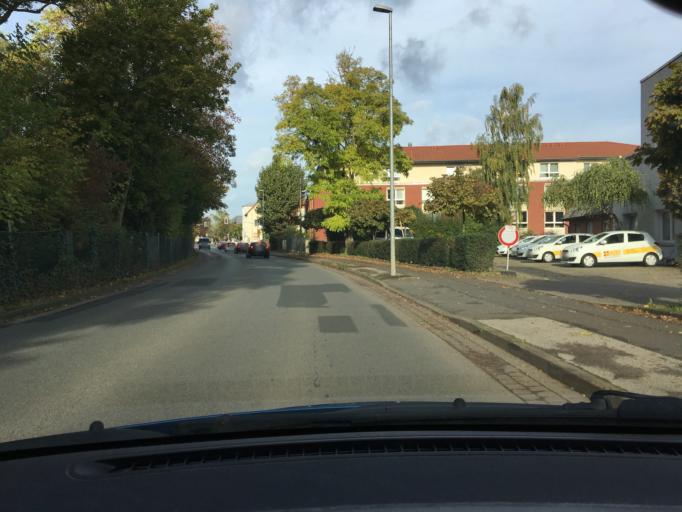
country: DE
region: Lower Saxony
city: Barsinghausen
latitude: 52.3034
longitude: 9.4681
